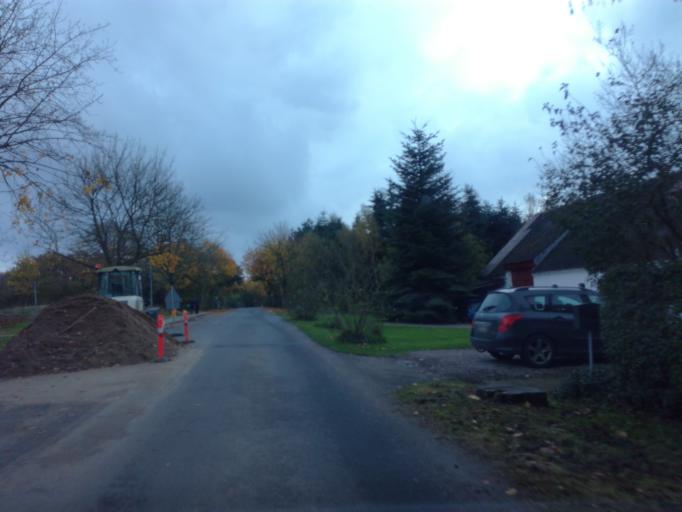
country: DK
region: South Denmark
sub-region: Vejle Kommune
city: Borkop
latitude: 55.6421
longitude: 9.6581
